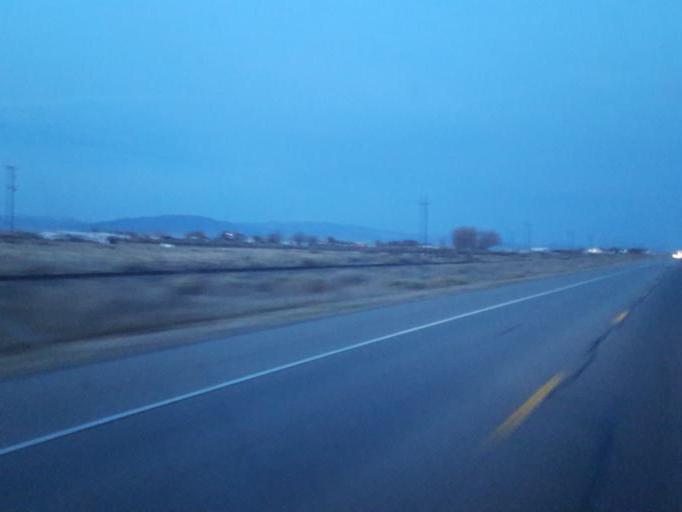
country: US
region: Colorado
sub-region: Alamosa County
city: Alamosa
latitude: 37.4954
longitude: -105.9423
